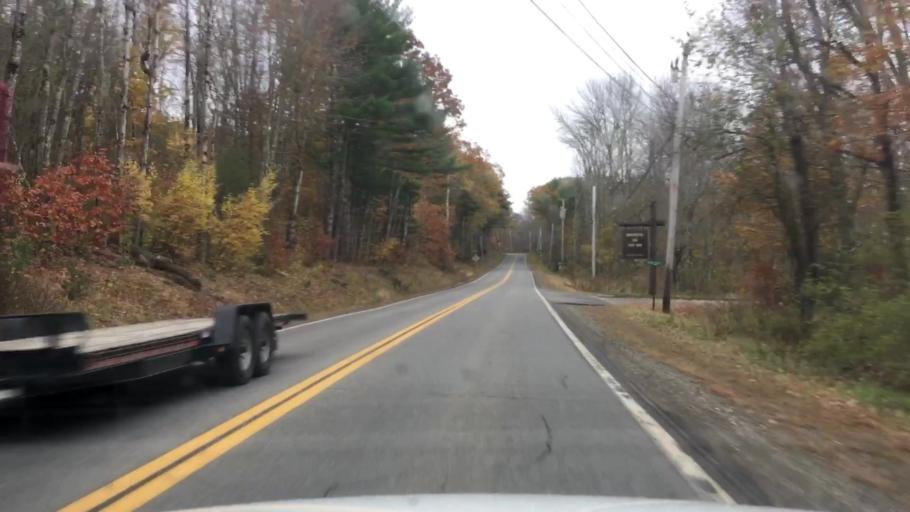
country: US
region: Maine
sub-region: Lincoln County
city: Jefferson
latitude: 44.1987
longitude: -69.4522
